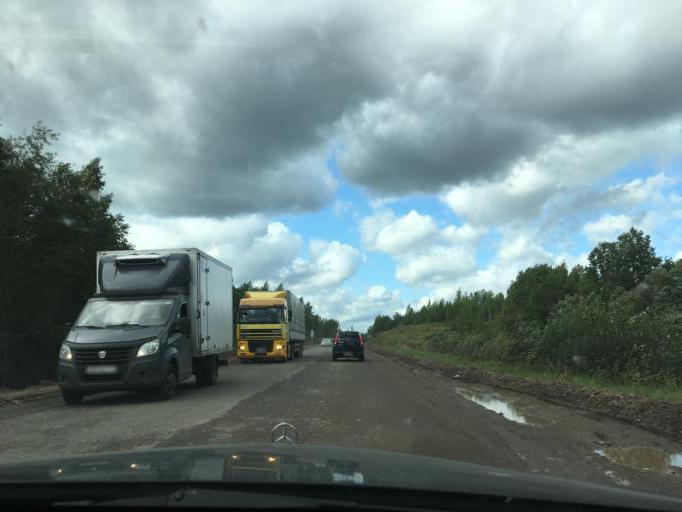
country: RU
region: Pskov
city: Novosokol'niki
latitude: 56.2928
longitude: 30.2390
